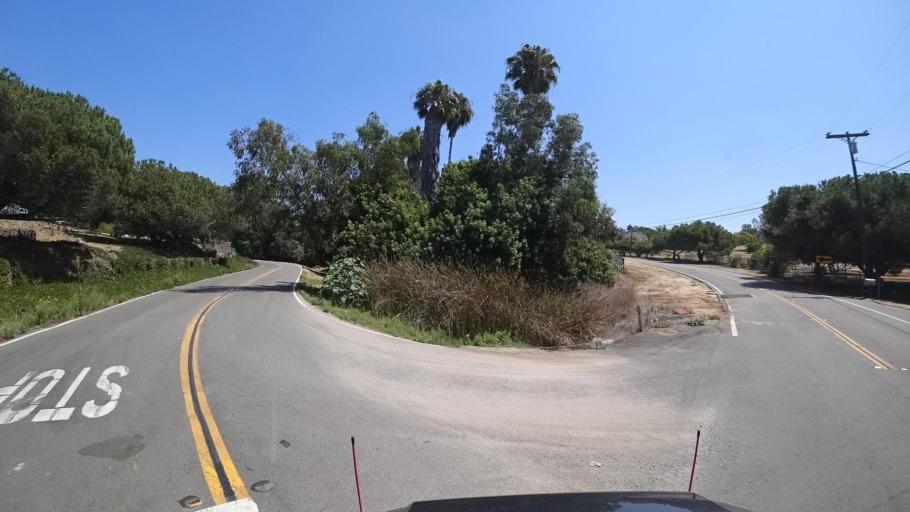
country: US
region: California
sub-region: San Diego County
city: Vista
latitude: 33.1821
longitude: -117.2674
